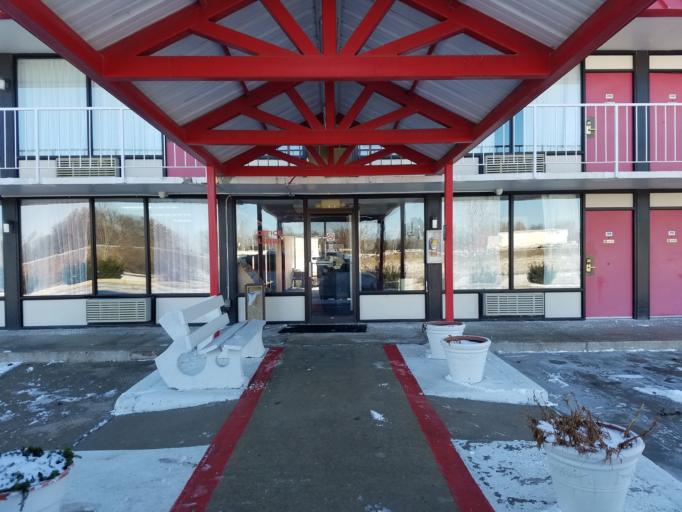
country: US
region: Missouri
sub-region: Jackson County
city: Oak Grove
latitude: 39.0149
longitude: -94.1246
